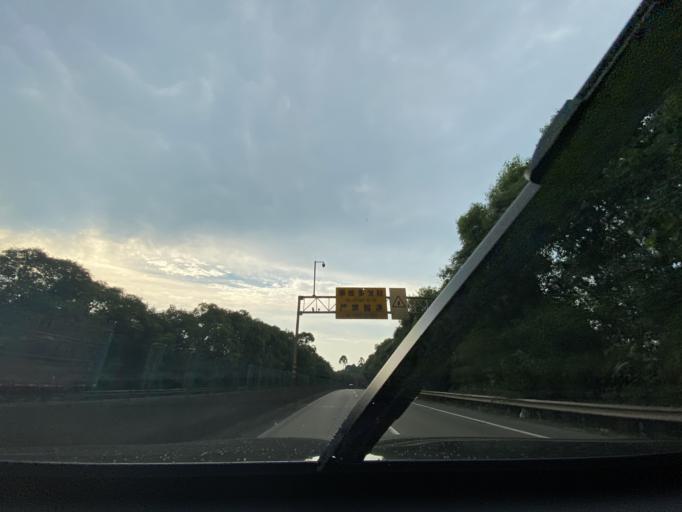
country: CN
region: Sichuan
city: Chonglong
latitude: 29.7901
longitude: 104.7277
